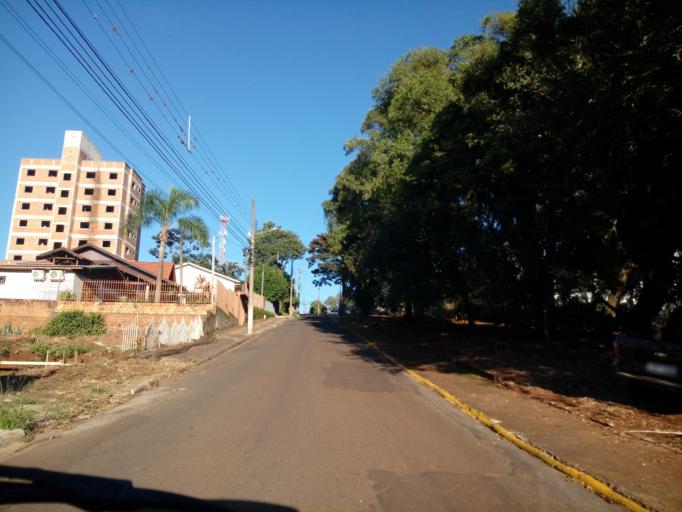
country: BR
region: Santa Catarina
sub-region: Chapeco
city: Chapeco
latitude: -27.1132
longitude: -52.6086
